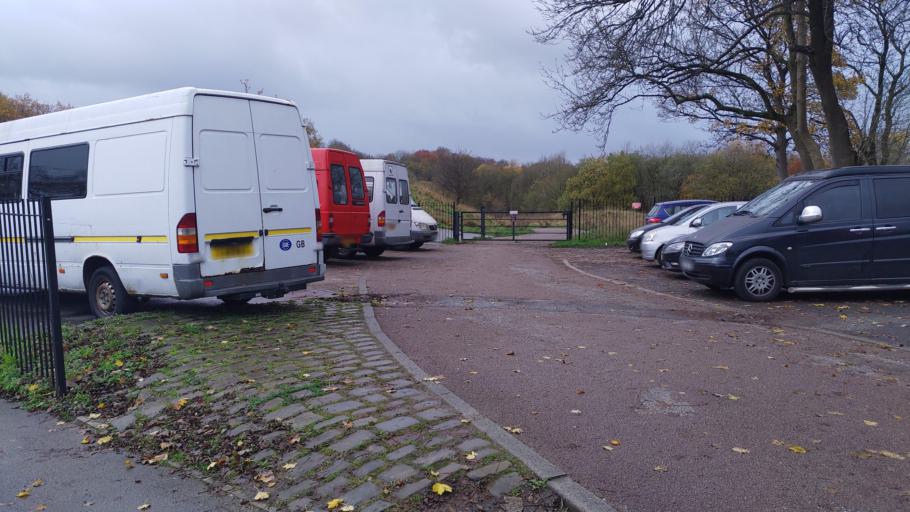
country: GB
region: England
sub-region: Borough of Rochdale
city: Rochdale
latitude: 53.6090
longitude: -2.1648
